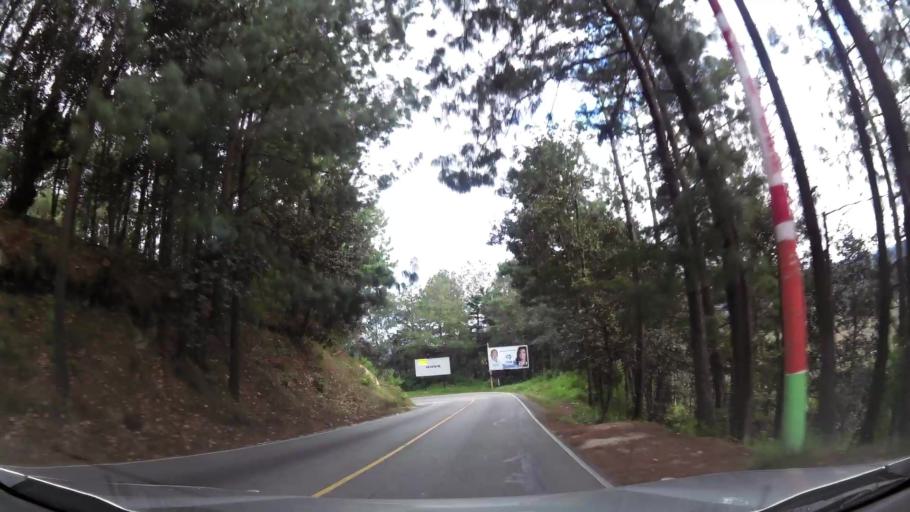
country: GT
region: Quiche
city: Chichicastenango
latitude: 14.8958
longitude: -91.1176
